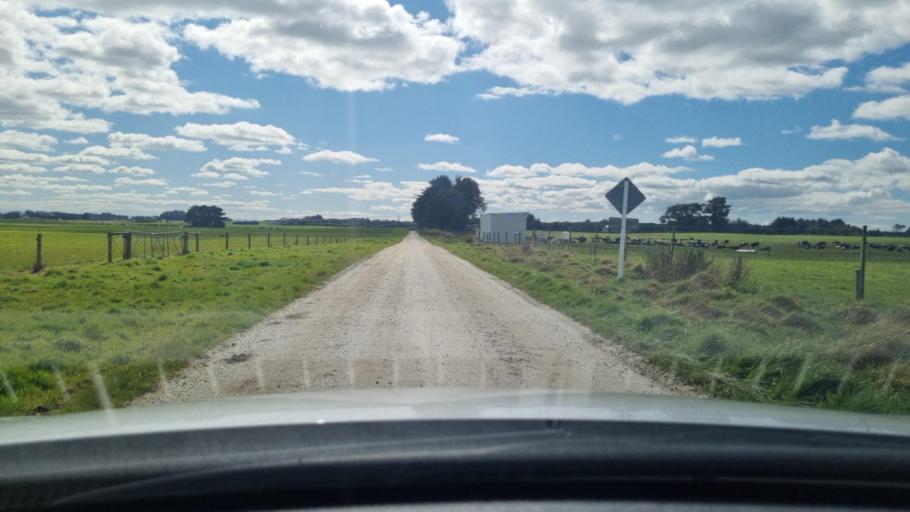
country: NZ
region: Southland
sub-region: Invercargill City
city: Invercargill
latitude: -46.4499
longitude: 168.4204
